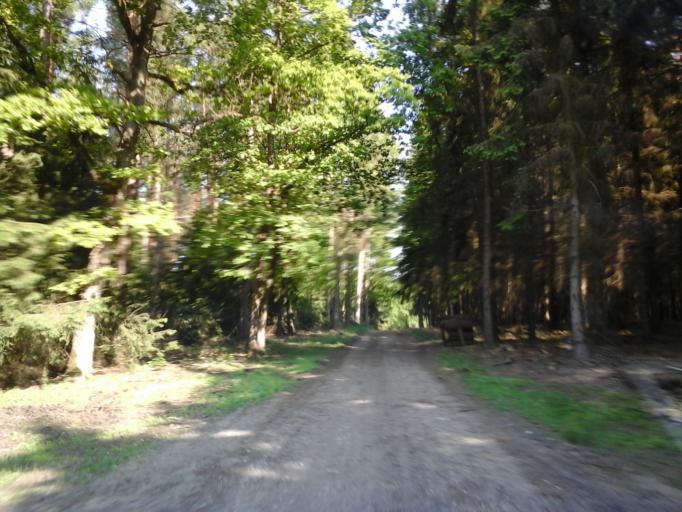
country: PL
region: West Pomeranian Voivodeship
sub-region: Powiat choszczenski
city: Recz
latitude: 53.3317
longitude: 15.5241
